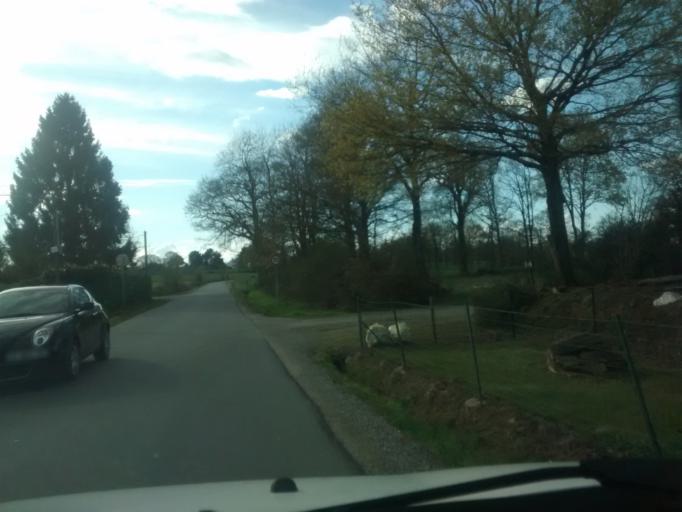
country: FR
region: Brittany
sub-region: Departement d'Ille-et-Vilaine
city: La Bouexiere
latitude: 48.1718
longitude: -1.4462
